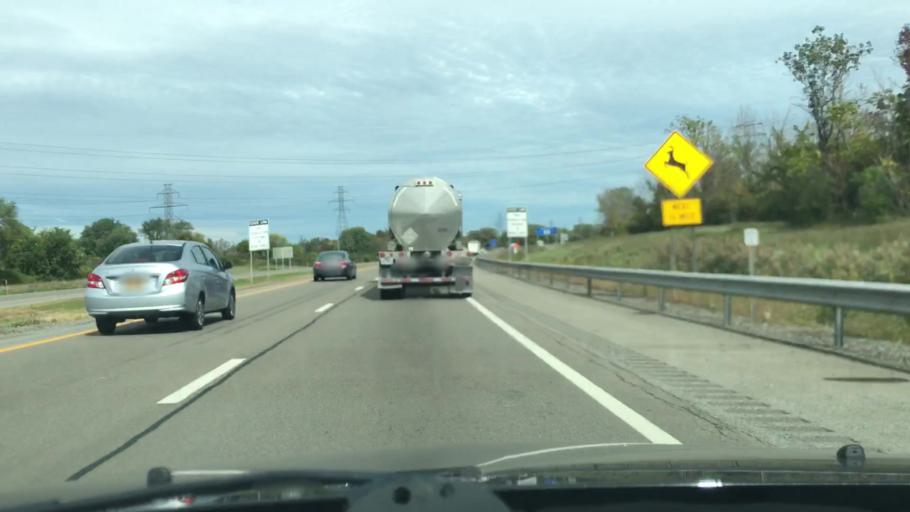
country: US
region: New York
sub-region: Erie County
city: Blasdell
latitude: 42.8014
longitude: -78.8147
